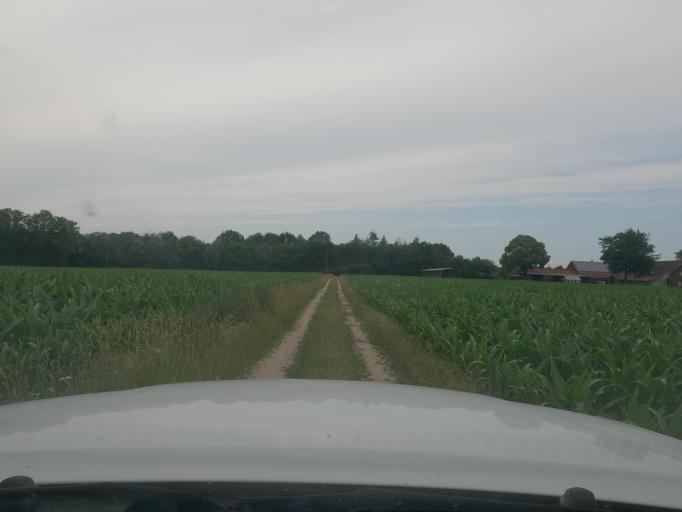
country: DE
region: North Rhine-Westphalia
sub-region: Regierungsbezirk Munster
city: Raesfeld
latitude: 51.7308
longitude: 6.8693
